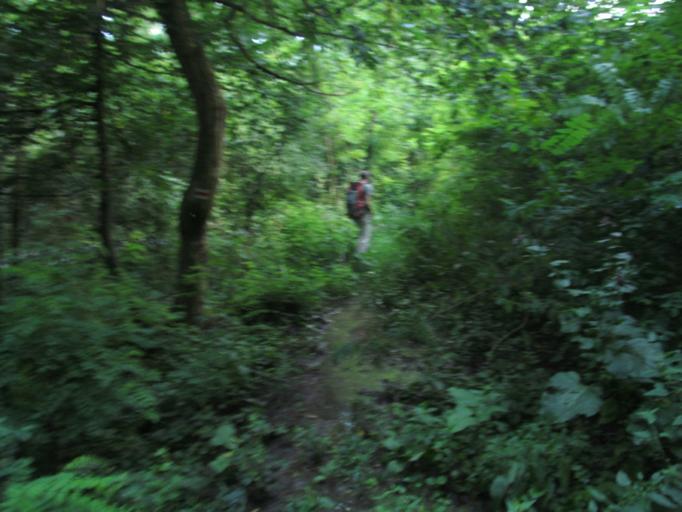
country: HU
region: Pest
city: Veroce
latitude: 47.8375
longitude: 19.0867
